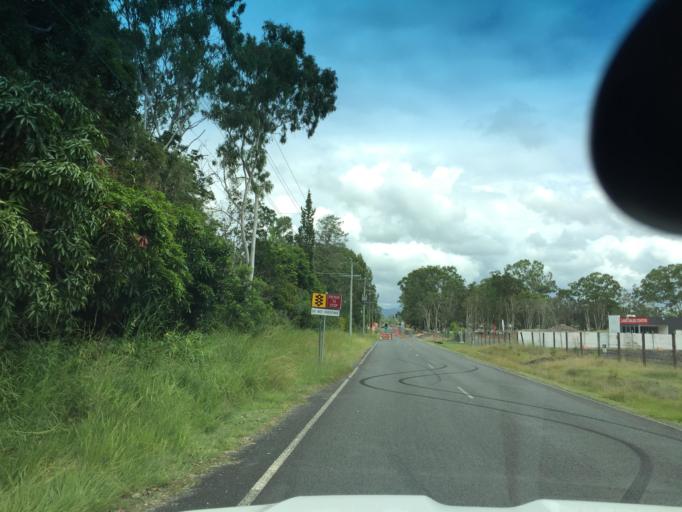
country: AU
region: Queensland
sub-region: Moreton Bay
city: Burpengary
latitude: -27.1654
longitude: 152.9888
